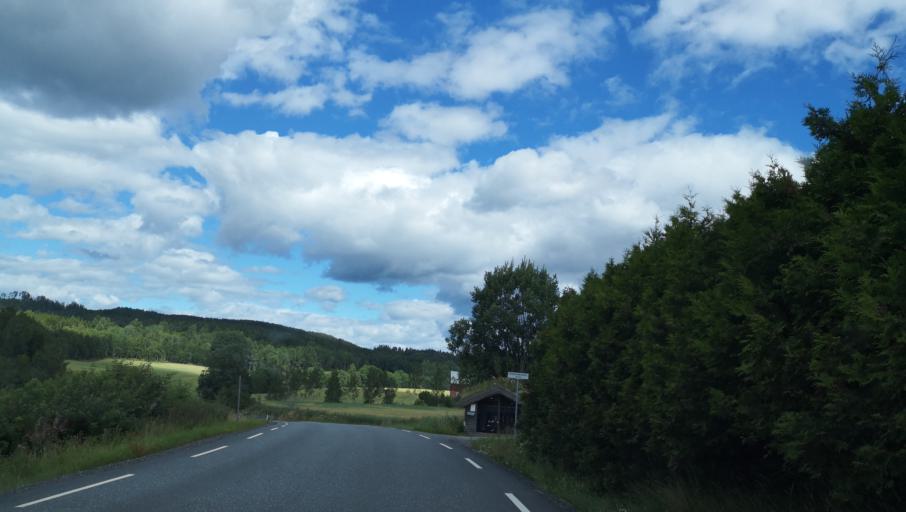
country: NO
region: Ostfold
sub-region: Hobol
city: Tomter
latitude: 59.6699
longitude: 11.0052
